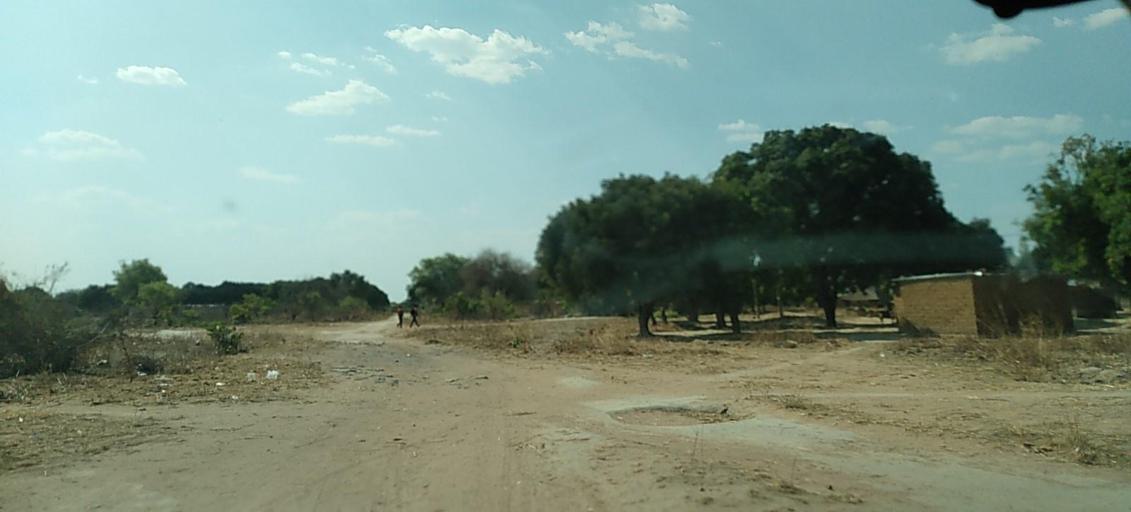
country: ZM
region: North-Western
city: Kalengwa
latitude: -13.1292
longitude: 25.0108
